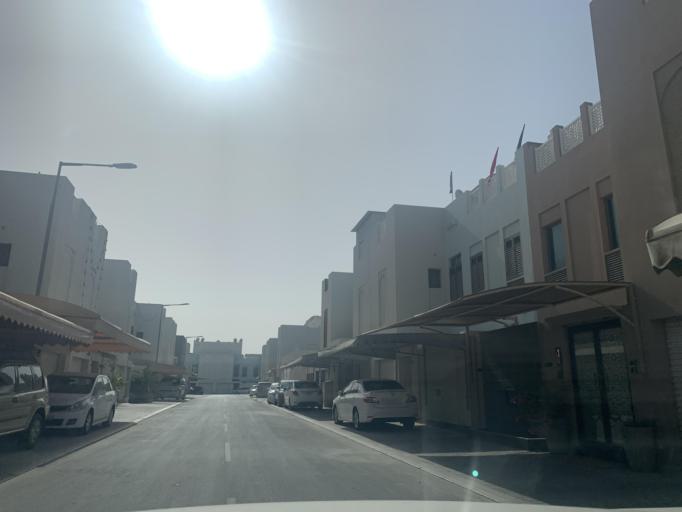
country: BH
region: Northern
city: Sitrah
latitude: 26.1584
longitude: 50.6271
